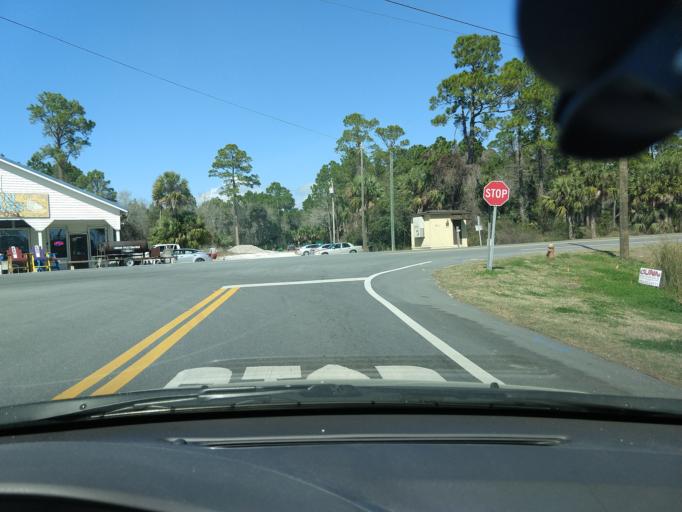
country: US
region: Florida
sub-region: Gulf County
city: Port Saint Joe
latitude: 29.6864
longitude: -85.2603
